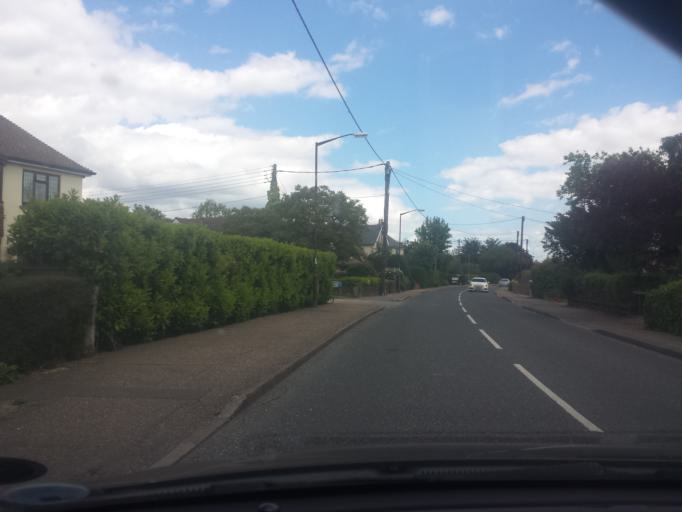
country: GB
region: England
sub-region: Essex
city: Little Clacton
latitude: 51.8587
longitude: 1.1673
